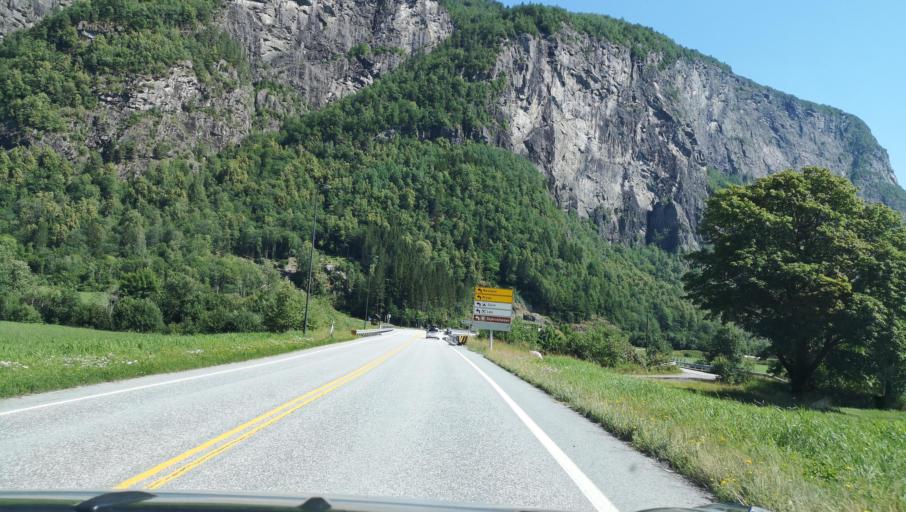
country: NO
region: Hordaland
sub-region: Granvin
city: Granvin
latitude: 60.5713
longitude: 6.6884
